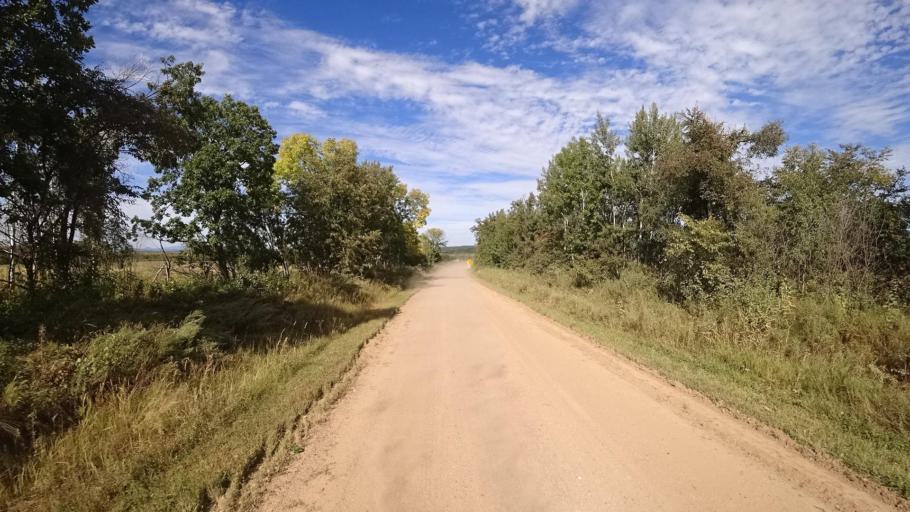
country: RU
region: Primorskiy
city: Yakovlevka
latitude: 44.4218
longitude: 133.5719
